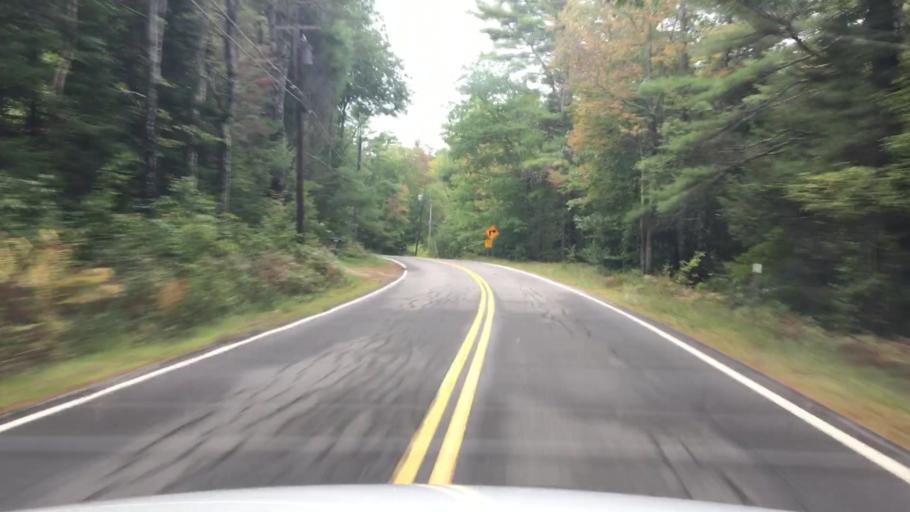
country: US
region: New Hampshire
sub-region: Carroll County
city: Effingham
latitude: 43.7323
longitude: -71.0049
